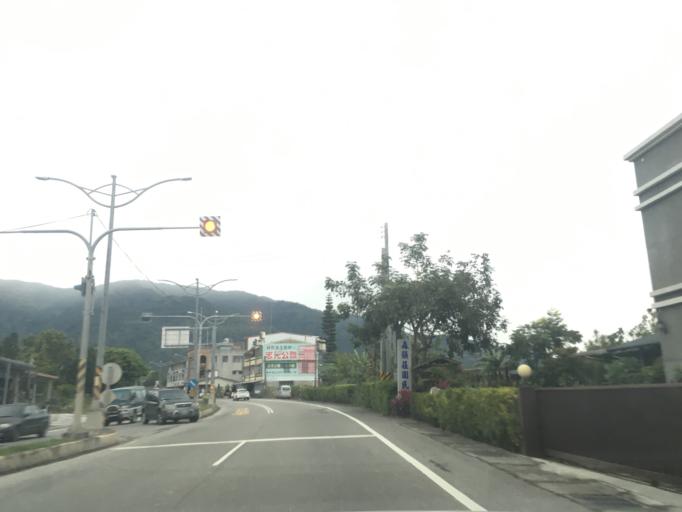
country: TW
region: Taiwan
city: Taitung City
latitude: 22.6940
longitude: 121.0458
